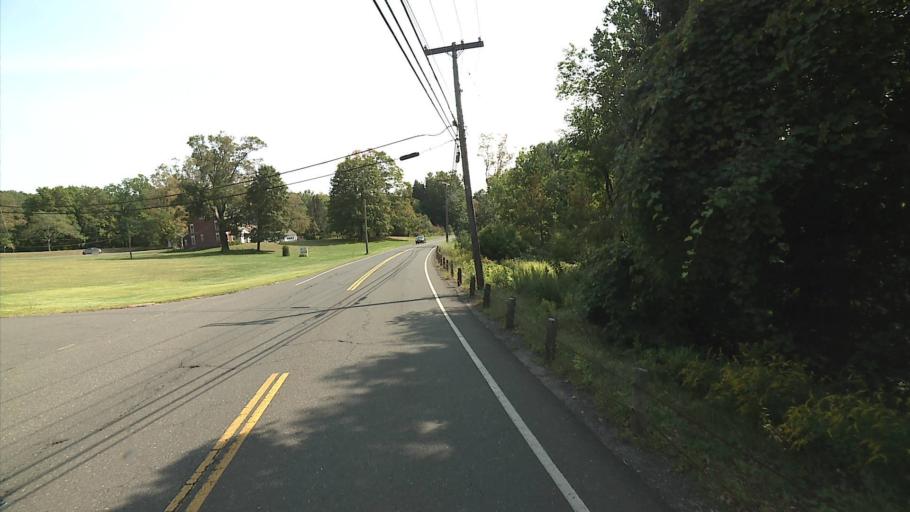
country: US
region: Connecticut
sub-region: New Haven County
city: Heritage Village
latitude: 41.4864
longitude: -73.2585
